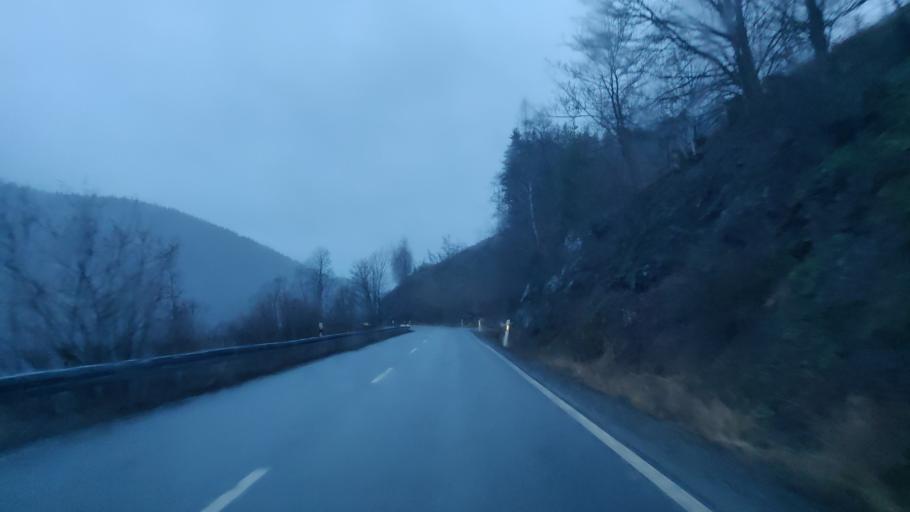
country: DE
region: Lower Saxony
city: Sankt Andreasberg
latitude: 51.6695
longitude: 10.5421
